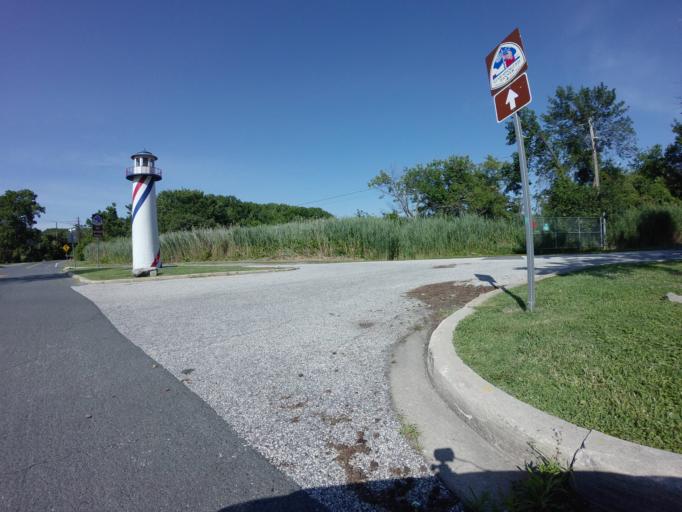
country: US
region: Maryland
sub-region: Baltimore County
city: Edgemere
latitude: 39.2031
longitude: -76.4456
